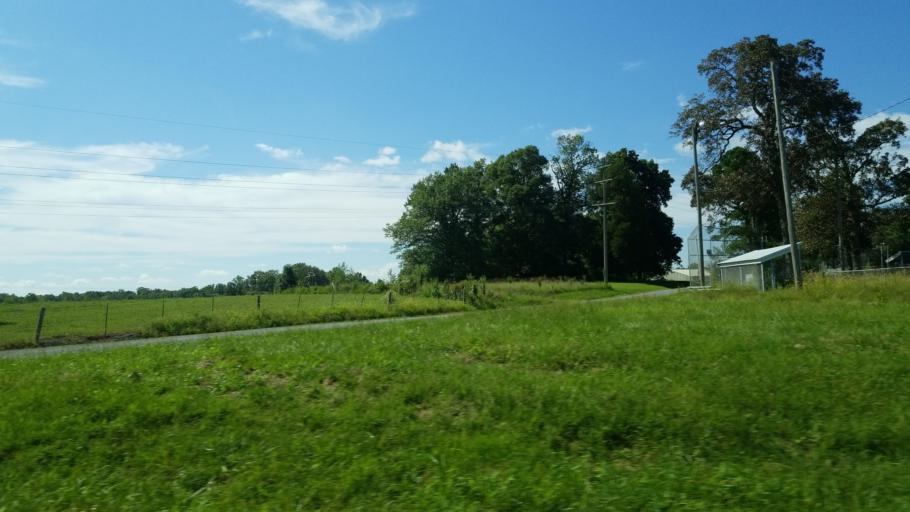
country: US
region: Illinois
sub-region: Williamson County
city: Marion
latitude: 37.7554
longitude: -88.8736
